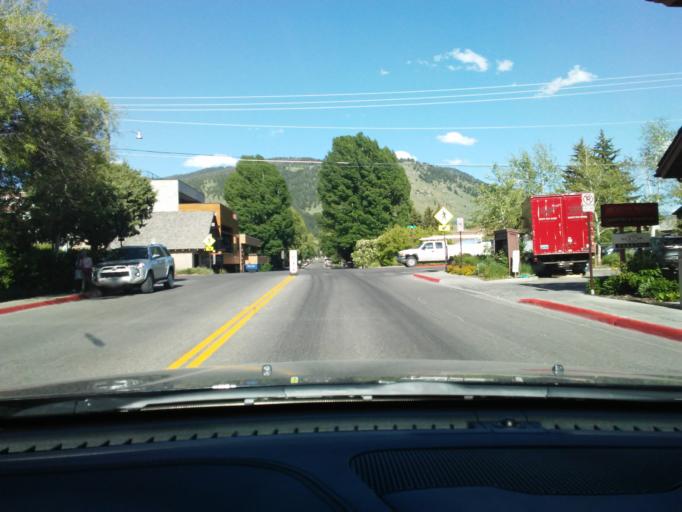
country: US
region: Wyoming
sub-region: Teton County
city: Jackson
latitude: 43.4785
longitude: -110.7611
